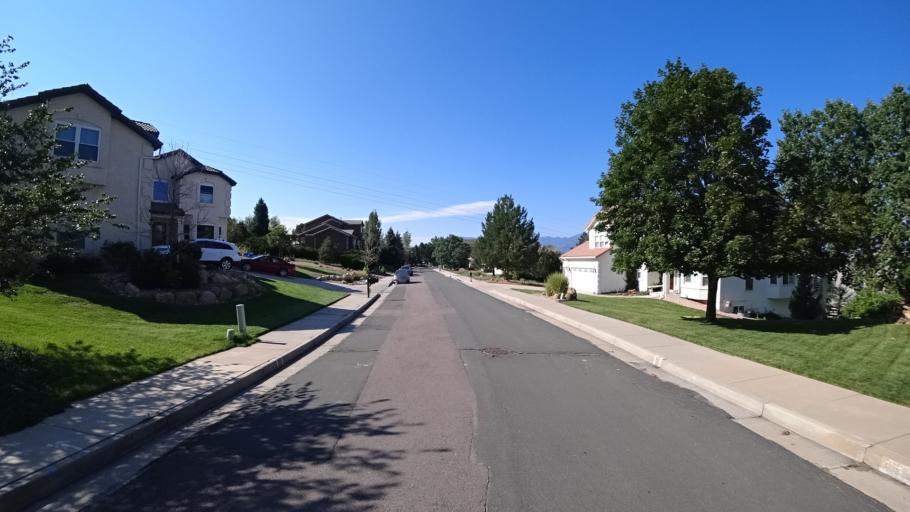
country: US
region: Colorado
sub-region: El Paso County
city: Colorado Springs
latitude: 38.8831
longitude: -104.7861
